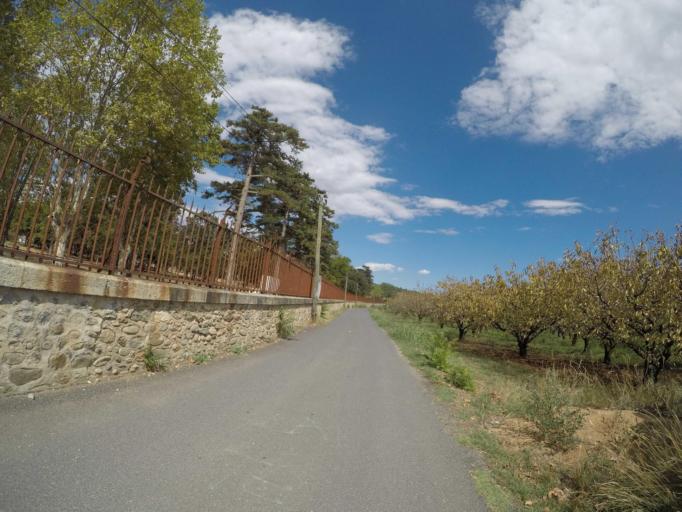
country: FR
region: Languedoc-Roussillon
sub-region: Departement des Pyrenees-Orientales
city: Sant Joan de Pladecorts
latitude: 42.5102
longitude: 2.7667
